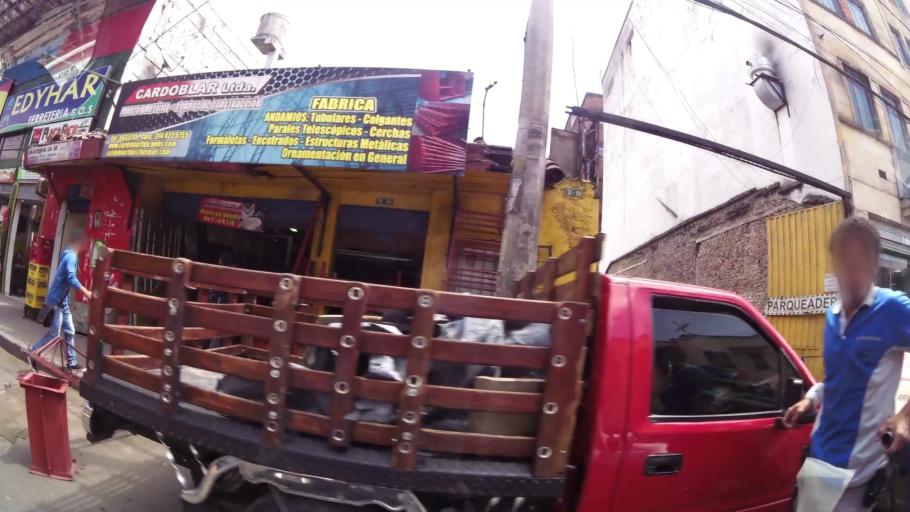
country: CO
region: Bogota D.C.
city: Bogota
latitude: 4.6038
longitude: -74.0819
